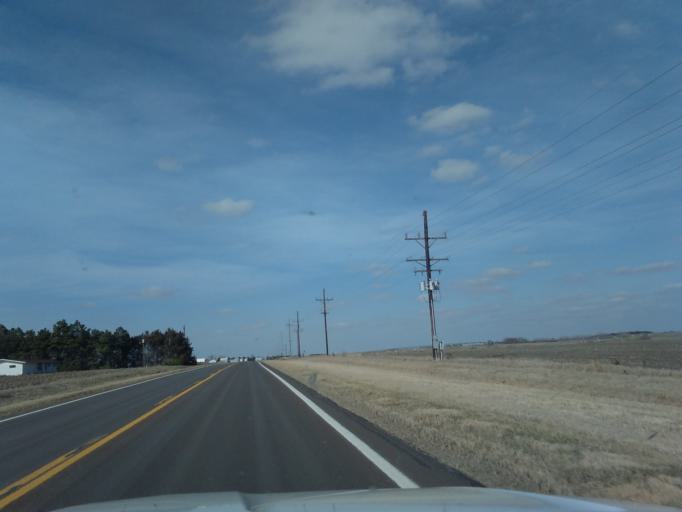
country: US
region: Nebraska
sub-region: Gage County
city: Beatrice
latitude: 40.1737
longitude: -96.9352
